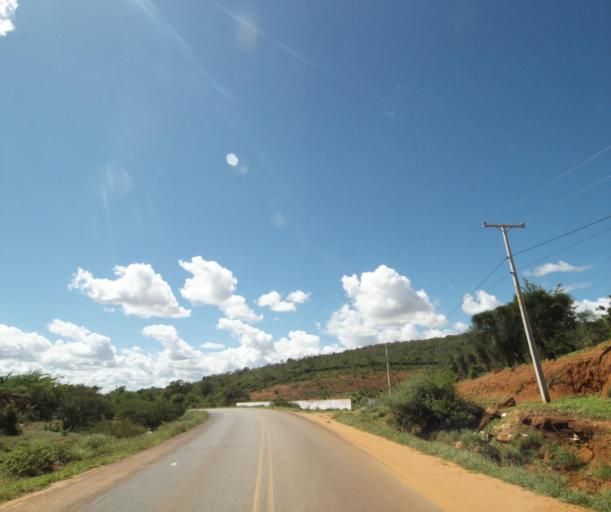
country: BR
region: Bahia
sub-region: Cacule
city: Cacule
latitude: -14.1986
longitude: -42.1360
